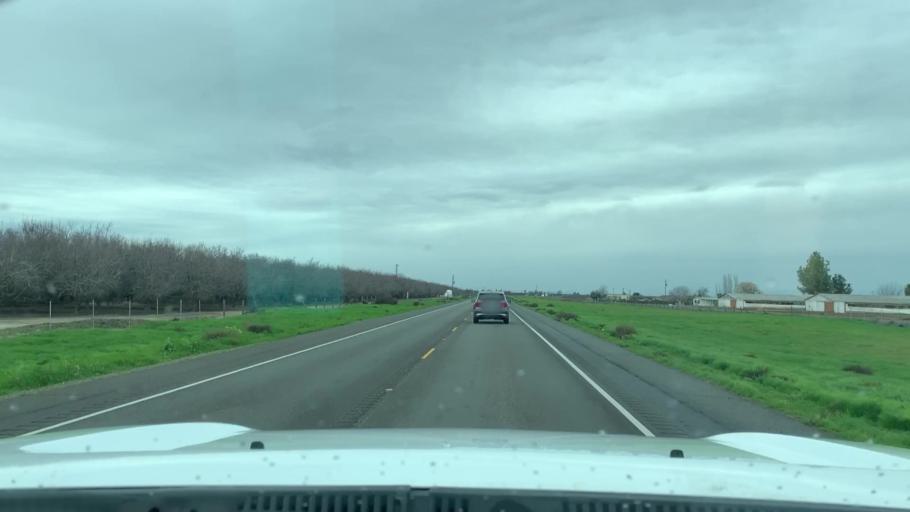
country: US
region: California
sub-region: Fresno County
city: Caruthers
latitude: 36.4782
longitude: -119.7928
